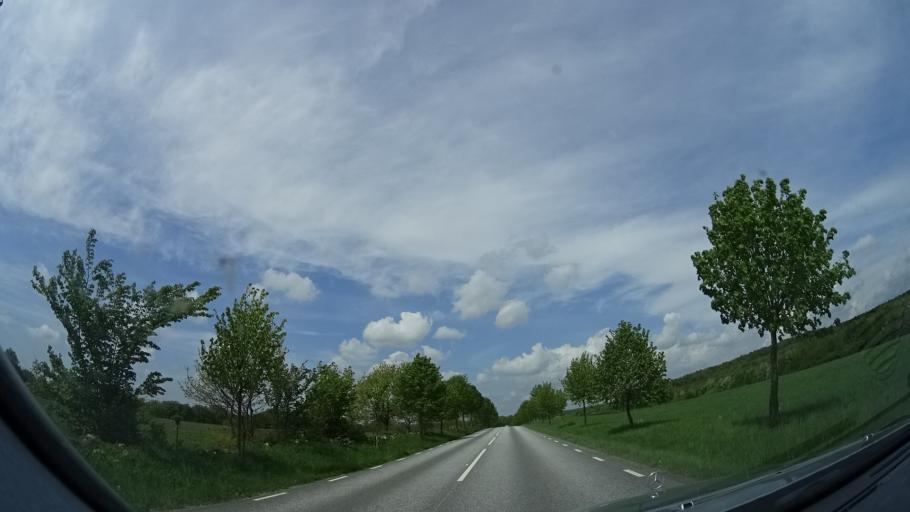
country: SE
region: Skane
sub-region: Sjobo Kommun
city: Sjoebo
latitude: 55.6682
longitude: 13.6684
